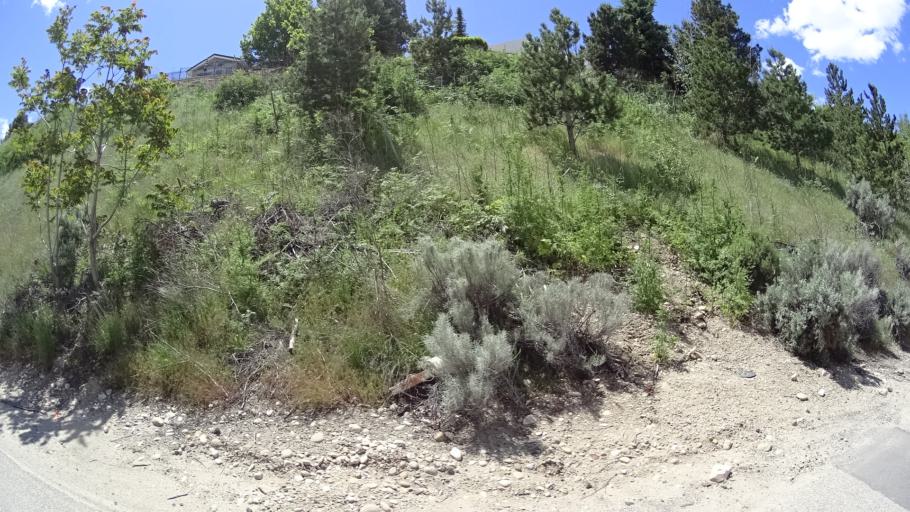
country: US
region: Idaho
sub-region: Ada County
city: Eagle
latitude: 43.6636
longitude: -116.3299
